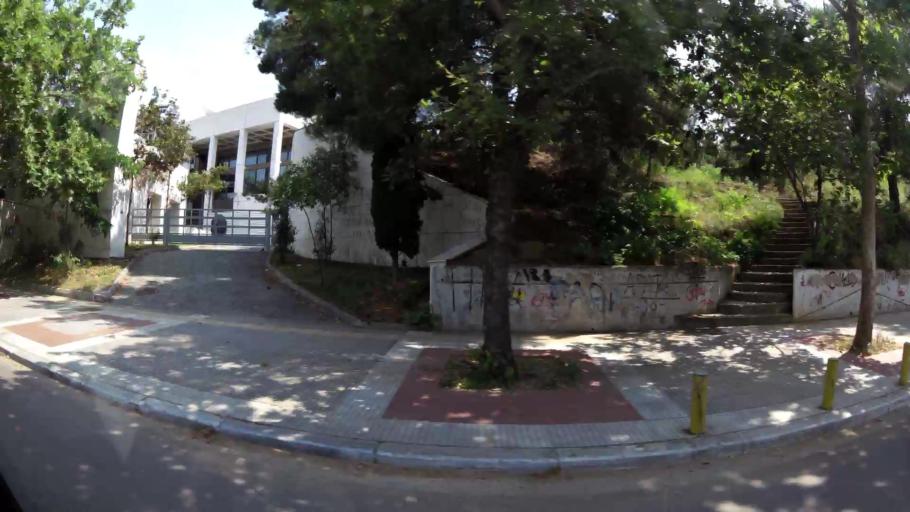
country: GR
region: Central Macedonia
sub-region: Nomos Thessalonikis
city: Agios Pavlos
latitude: 40.6320
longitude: 22.9605
